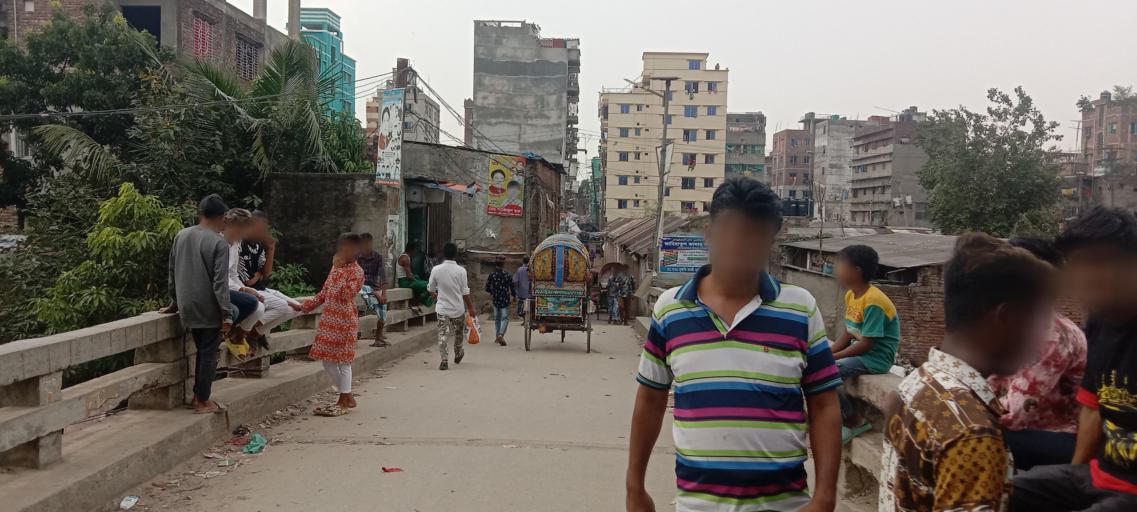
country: BD
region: Dhaka
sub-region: Dhaka
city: Dhaka
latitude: 23.6979
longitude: 90.4103
